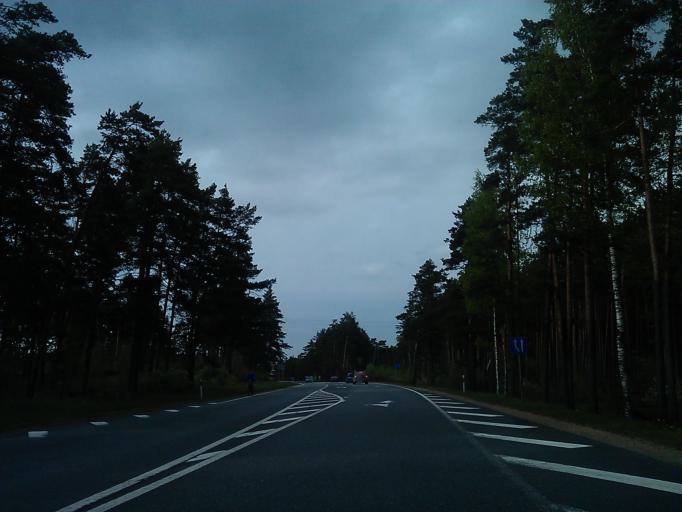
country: LV
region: Riga
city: Bergi
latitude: 57.0284
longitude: 24.3208
